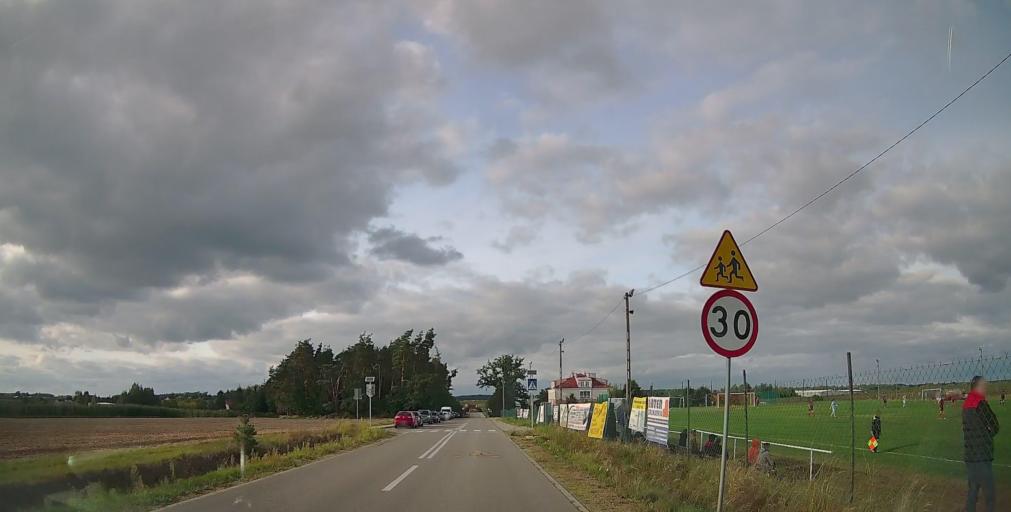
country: PL
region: Masovian Voivodeship
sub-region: Powiat bialobrzeski
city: Promna
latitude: 51.7519
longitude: 20.9619
